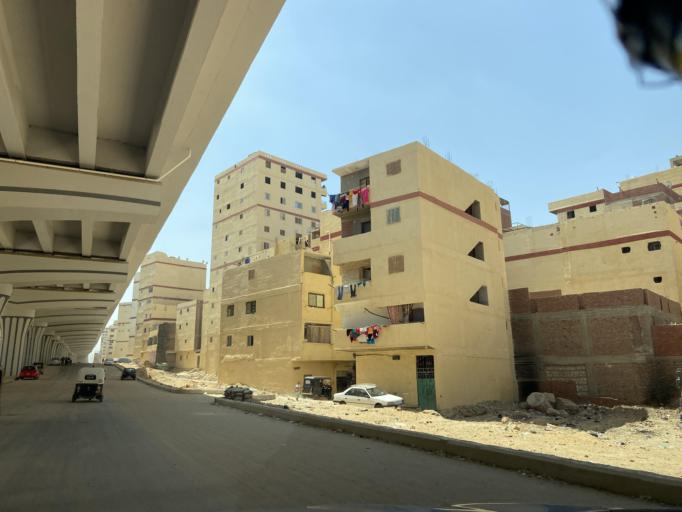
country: EG
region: Muhafazat al Qahirah
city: Cairo
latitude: 30.0672
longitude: 31.3841
